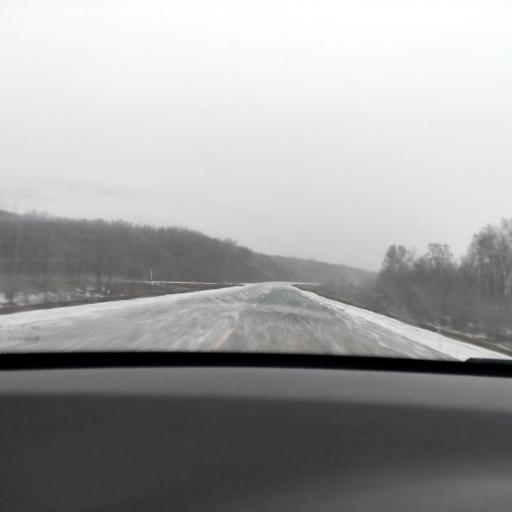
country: RU
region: Samara
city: Novokuybyshevsk
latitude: 52.9445
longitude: 49.8973
